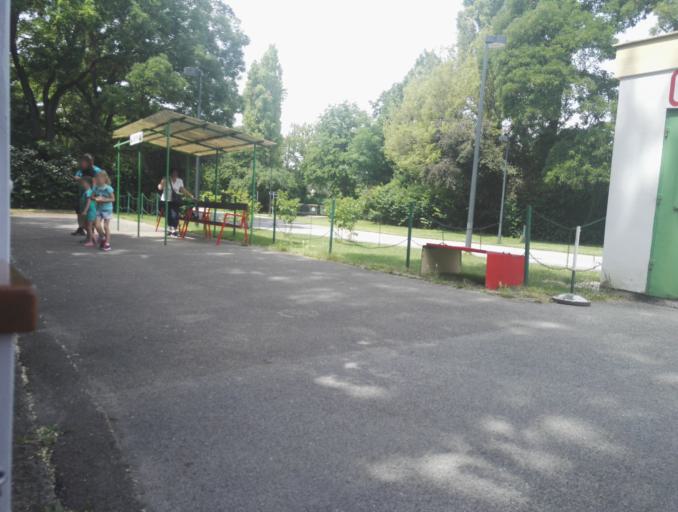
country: AT
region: Vienna
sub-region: Wien Stadt
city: Vienna
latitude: 48.2401
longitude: 16.4090
